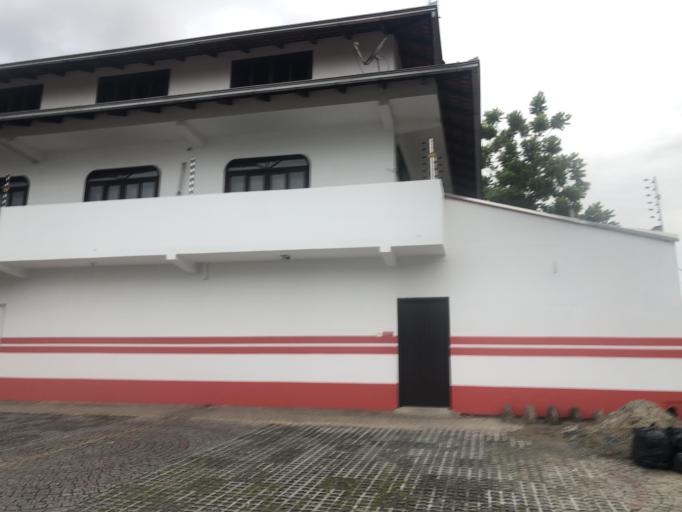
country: BR
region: Santa Catarina
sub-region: Joinville
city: Joinville
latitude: -26.3223
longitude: -48.8338
